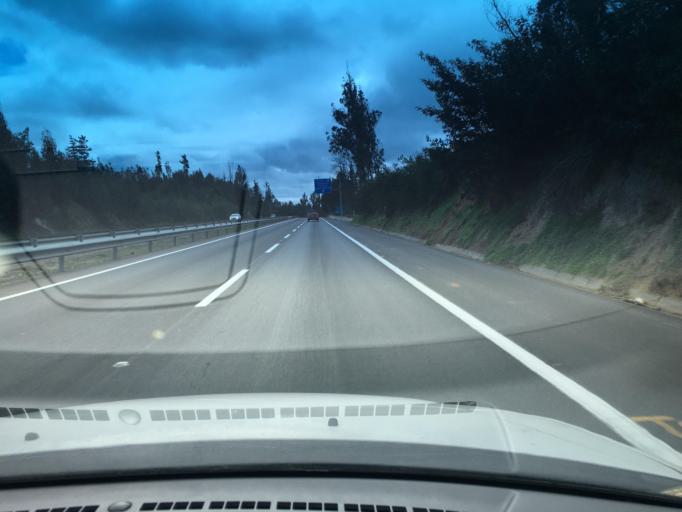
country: CL
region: Valparaiso
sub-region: Provincia de Valparaiso
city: Vina del Mar
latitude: -33.1564
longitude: -71.5513
